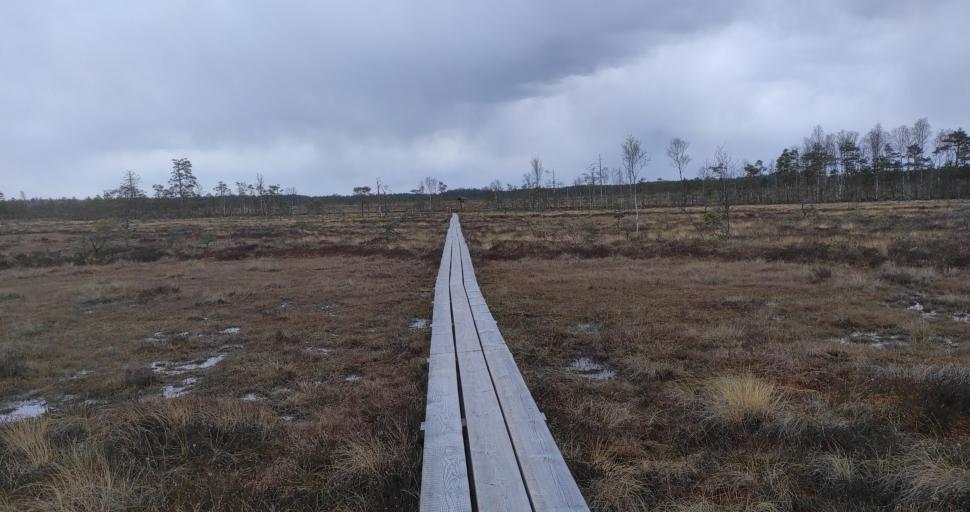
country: LV
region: Dundaga
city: Dundaga
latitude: 57.3453
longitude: 22.1566
